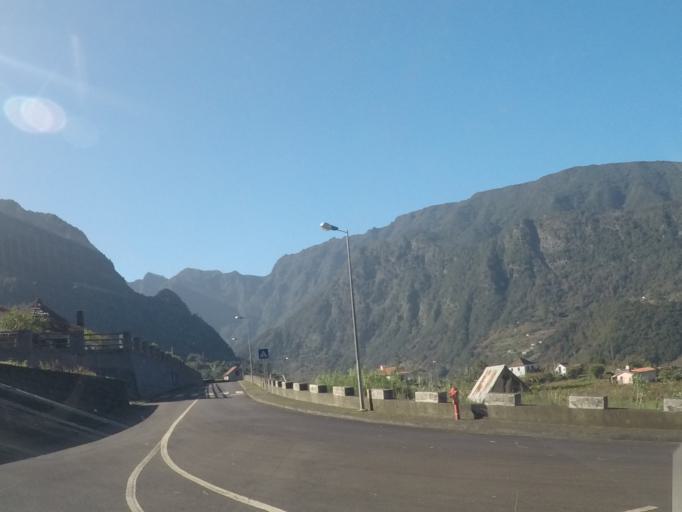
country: PT
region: Madeira
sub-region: Santana
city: Santana
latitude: 32.8015
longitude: -16.9591
